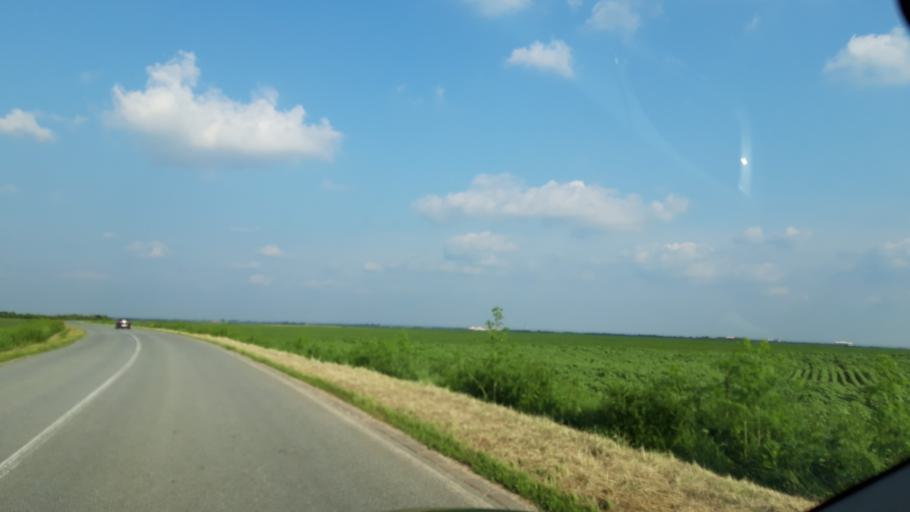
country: RS
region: Autonomna Pokrajina Vojvodina
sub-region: Sremski Okrug
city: Ingija
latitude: 45.0884
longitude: 20.1022
